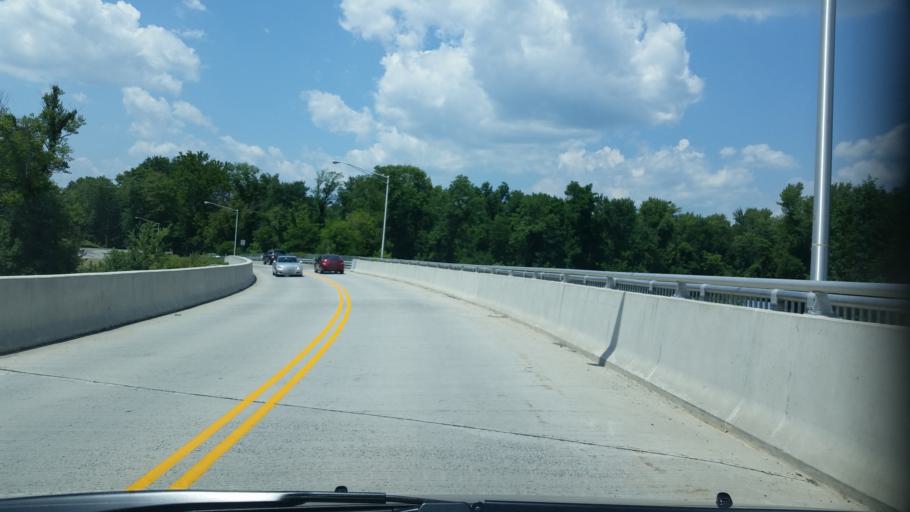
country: US
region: Pennsylvania
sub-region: Dauphin County
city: Hershey
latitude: 40.2871
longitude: -76.6776
